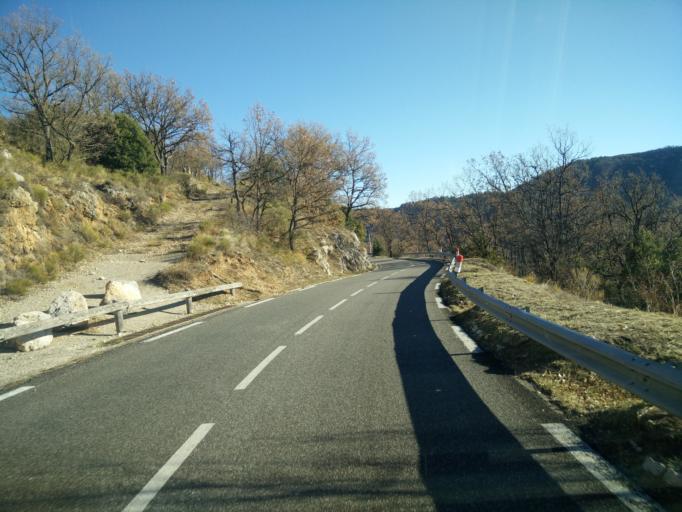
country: FR
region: Provence-Alpes-Cote d'Azur
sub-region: Departement des Alpes-Maritimes
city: Saint-Vallier-de-Thiey
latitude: 43.7193
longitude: 6.8267
